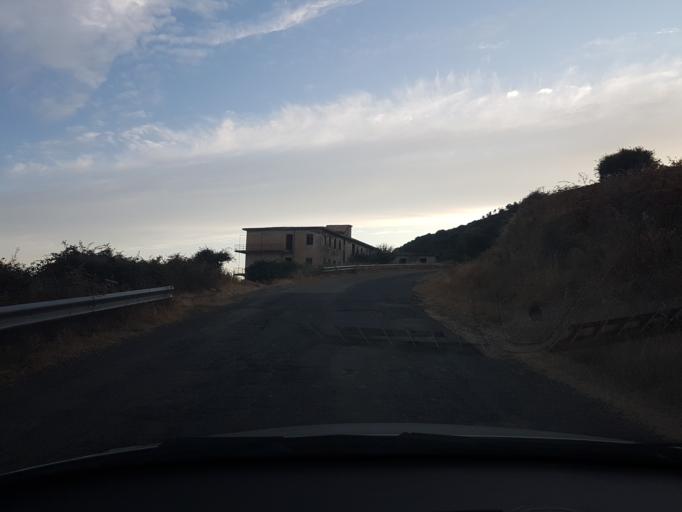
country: IT
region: Sardinia
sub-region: Provincia di Oristano
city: Seneghe
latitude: 40.1104
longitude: 8.6113
